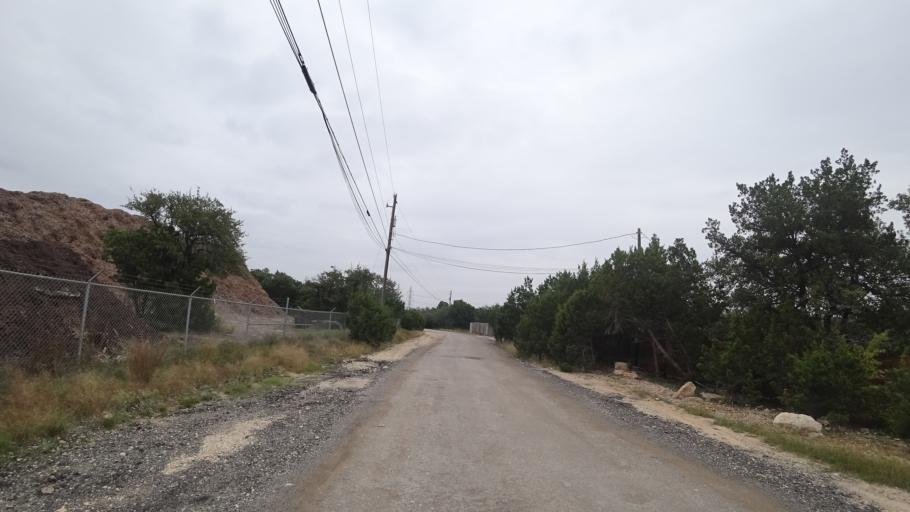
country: US
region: Texas
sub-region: Travis County
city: Hudson Bend
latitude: 30.3814
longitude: -97.9390
